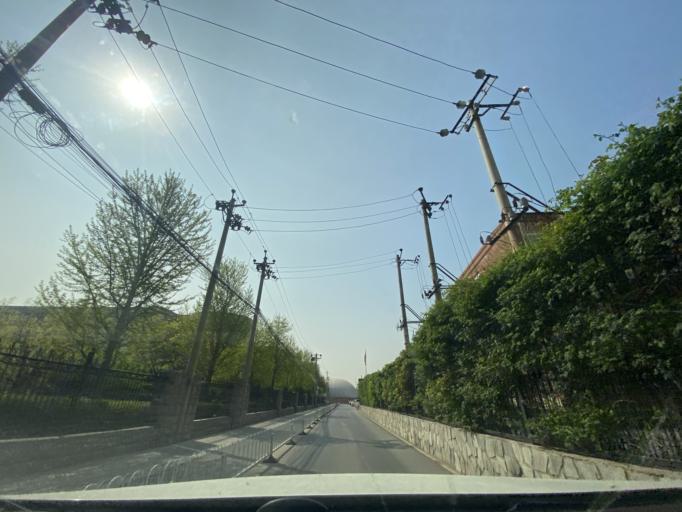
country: CN
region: Beijing
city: Sijiqing
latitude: 39.9437
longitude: 116.2511
